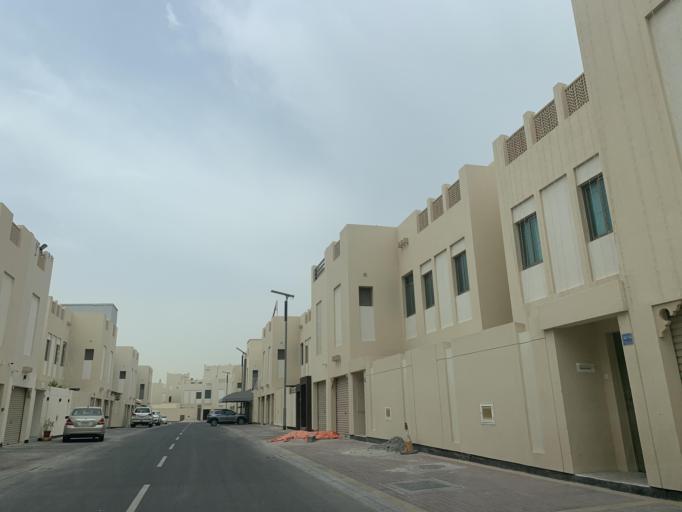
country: BH
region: Northern
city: Madinat `Isa
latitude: 26.1767
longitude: 50.5151
